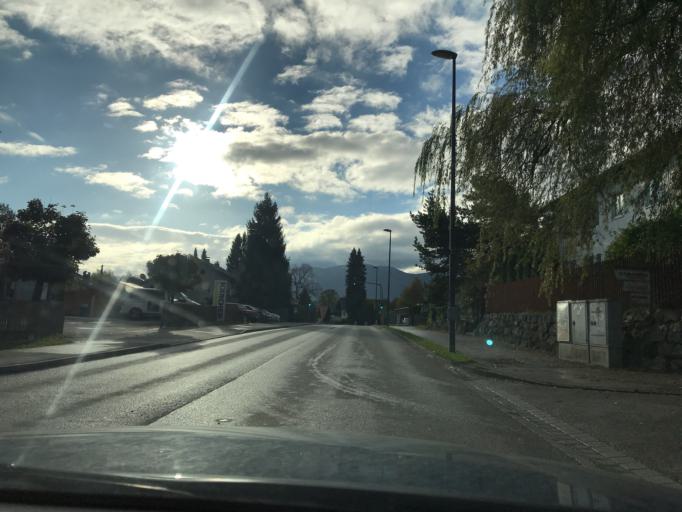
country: DE
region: Bavaria
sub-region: Upper Bavaria
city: Bad Toelz
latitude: 47.7688
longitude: 11.5589
